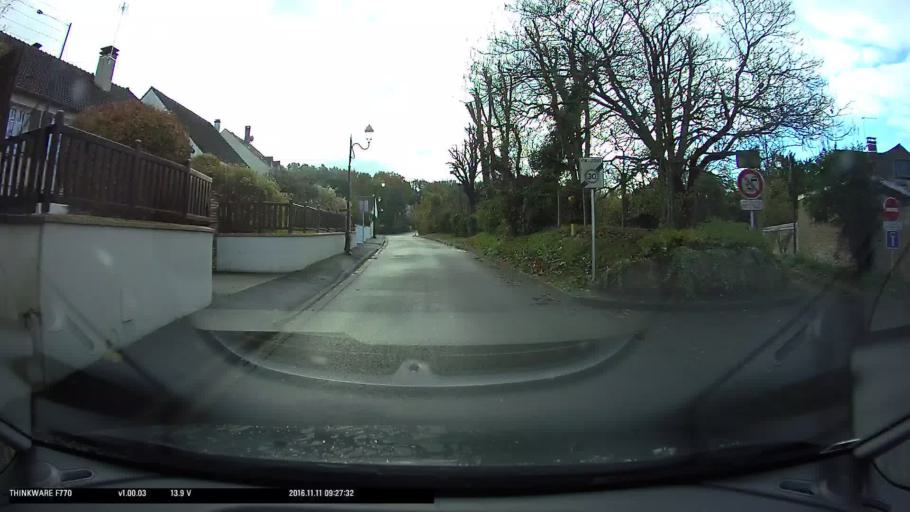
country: FR
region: Ile-de-France
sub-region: Departement du Val-d'Oise
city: Osny
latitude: 49.0752
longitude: 2.0373
